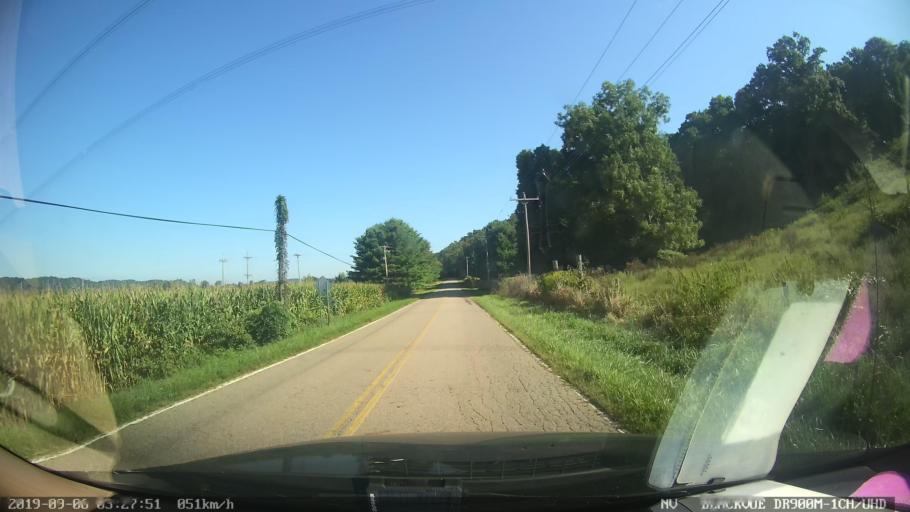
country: US
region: Ohio
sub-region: Licking County
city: Utica
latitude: 40.1553
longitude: -82.4070
